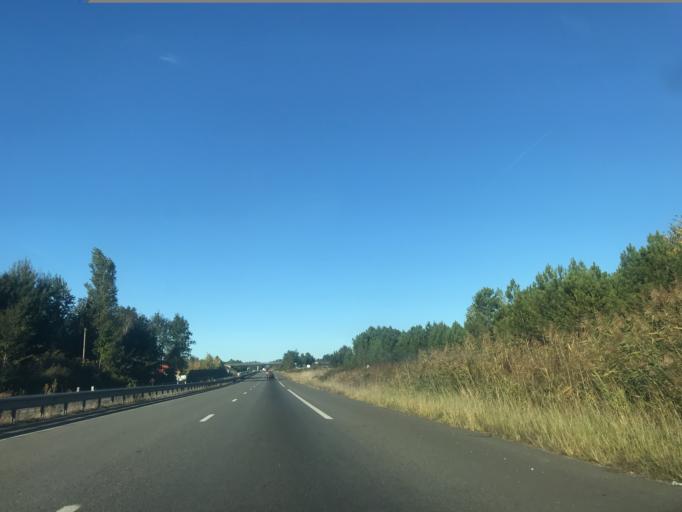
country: FR
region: Poitou-Charentes
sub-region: Departement de la Charente-Maritime
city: Montlieu-la-Garde
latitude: 45.2006
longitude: -0.3037
